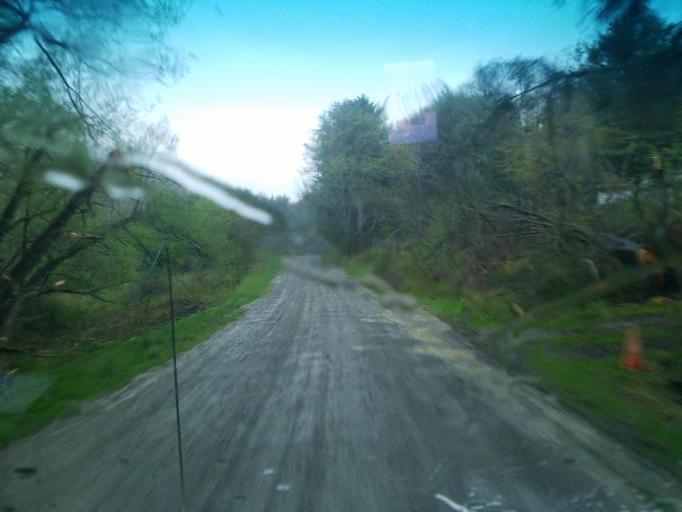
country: US
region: Pennsylvania
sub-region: Tioga County
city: Westfield
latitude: 41.8921
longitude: -77.7053
